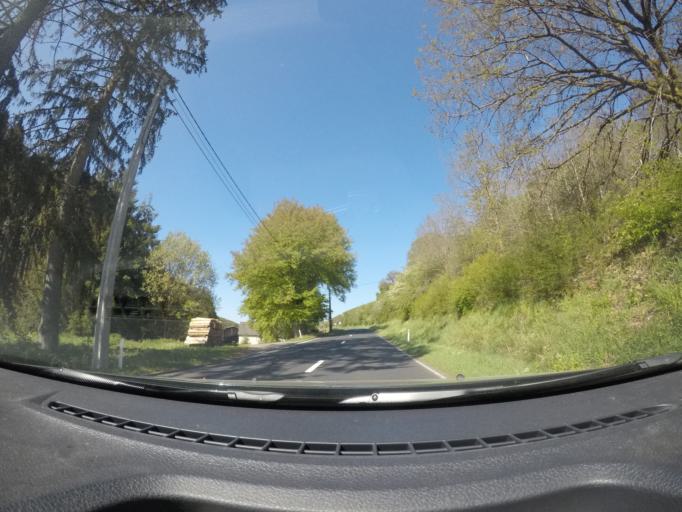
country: BE
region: Wallonia
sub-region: Province du Luxembourg
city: Fauvillers
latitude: 49.8523
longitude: 5.6948
